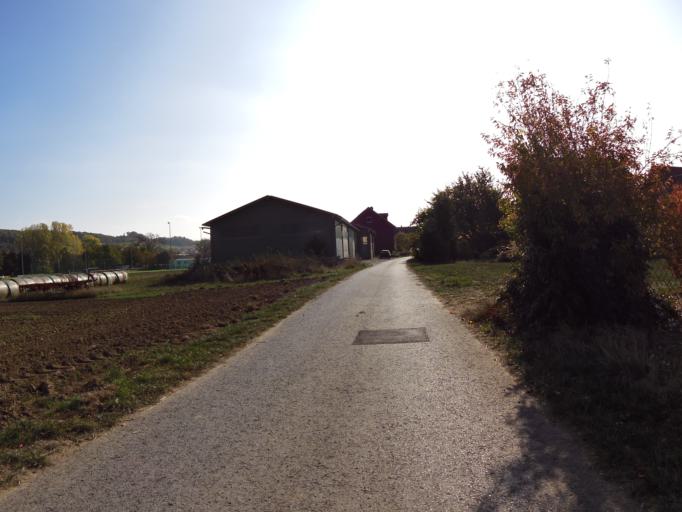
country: DE
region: Bavaria
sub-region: Regierungsbezirk Unterfranken
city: Winterhausen
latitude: 49.7106
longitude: 10.0145
